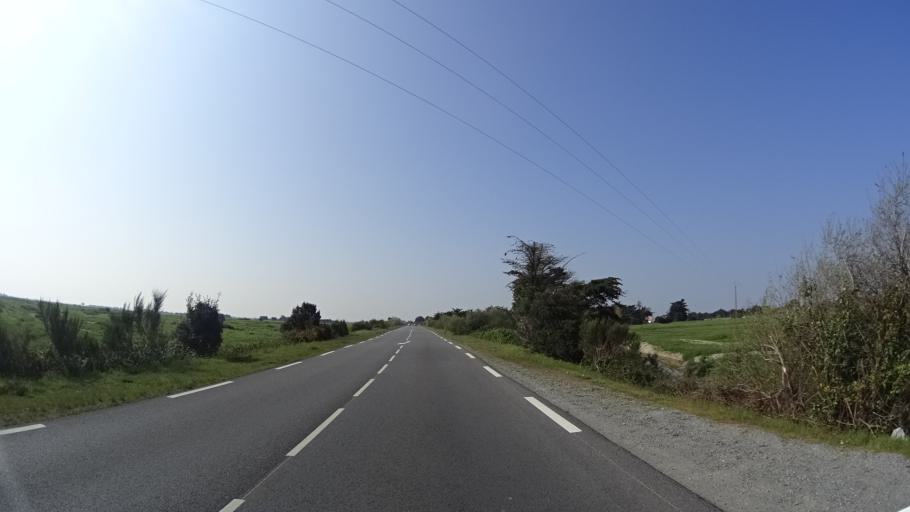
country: FR
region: Pays de la Loire
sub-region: Departement de la Loire-Atlantique
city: Bourgneuf-en-Retz
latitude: 47.0369
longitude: -1.9612
